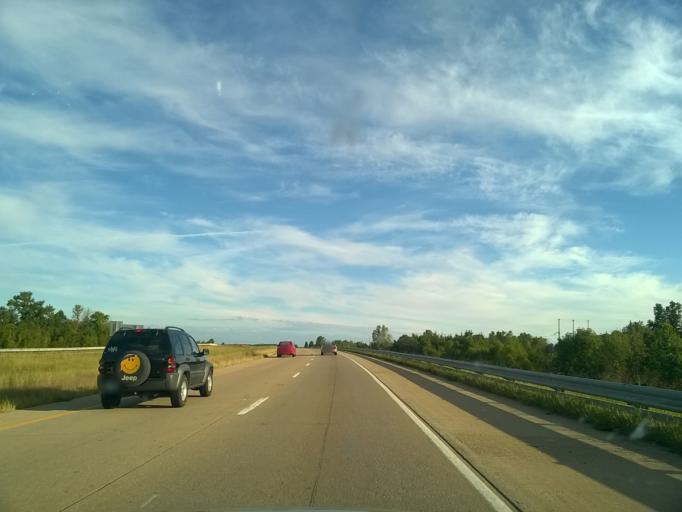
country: US
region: Indiana
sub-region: Vanderburgh County
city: Melody Hill
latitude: 38.1105
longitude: -87.4766
